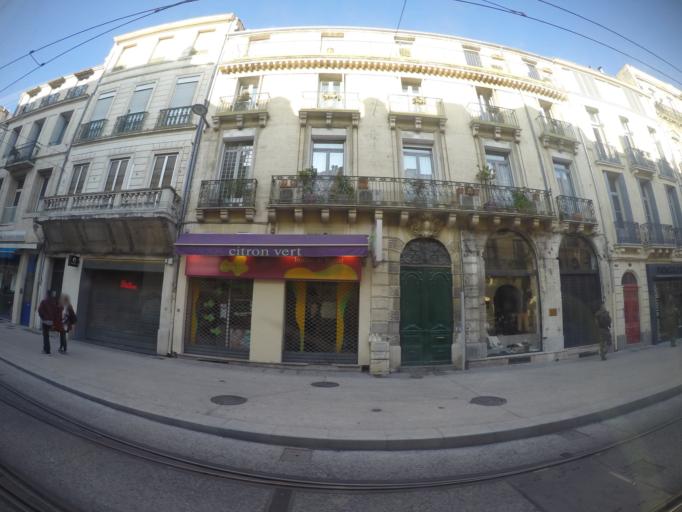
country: FR
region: Languedoc-Roussillon
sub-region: Departement de l'Herault
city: Montpellier
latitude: 43.6072
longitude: 3.8747
